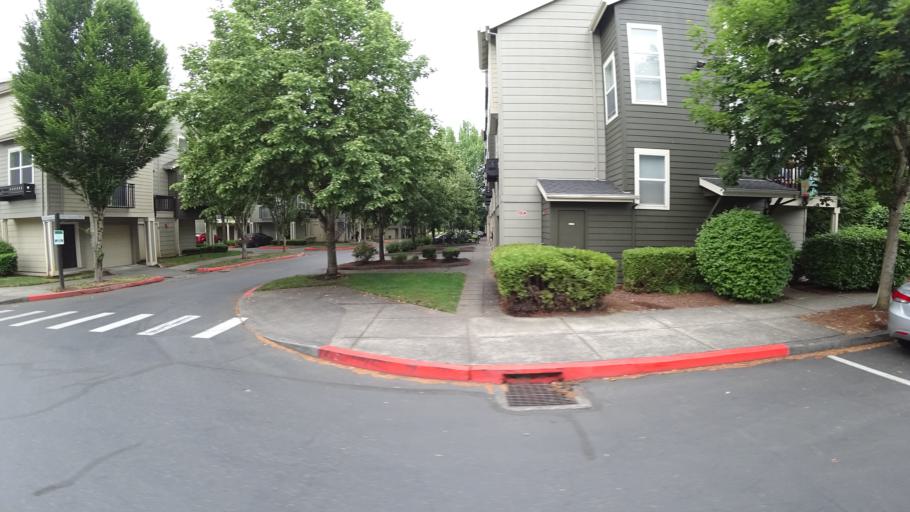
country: US
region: Oregon
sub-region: Washington County
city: Rockcreek
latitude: 45.5397
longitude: -122.8798
